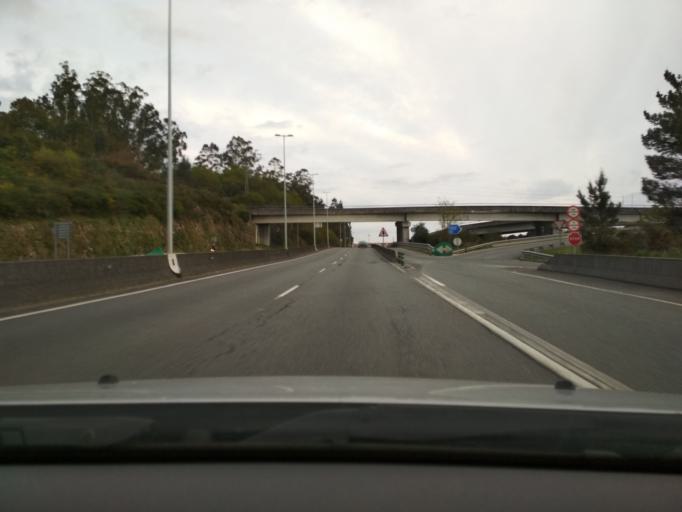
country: ES
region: Galicia
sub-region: Provincia da Coruna
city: Santiago de Compostela
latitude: 42.8541
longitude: -8.5715
